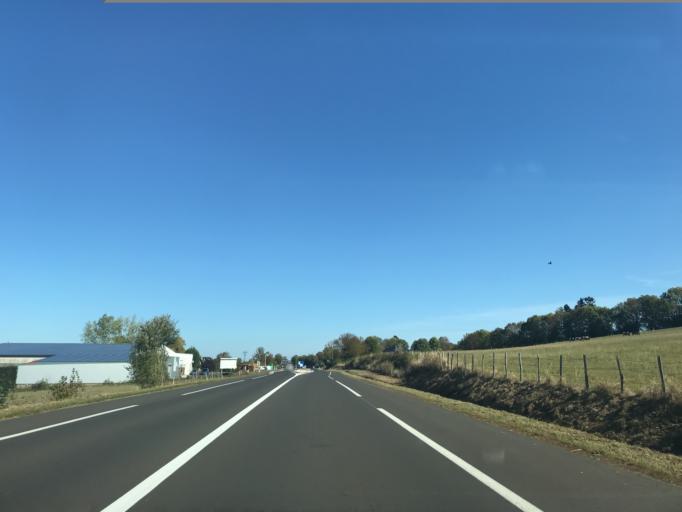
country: FR
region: Auvergne
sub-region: Departement du Puy-de-Dome
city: Gelles
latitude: 45.6995
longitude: 2.8060
